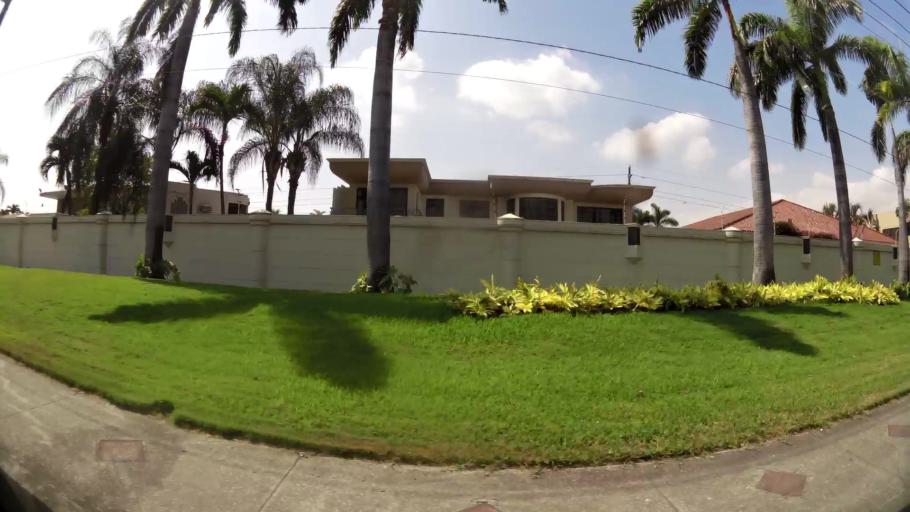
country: EC
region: Guayas
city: Eloy Alfaro
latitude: -2.1292
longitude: -79.8628
